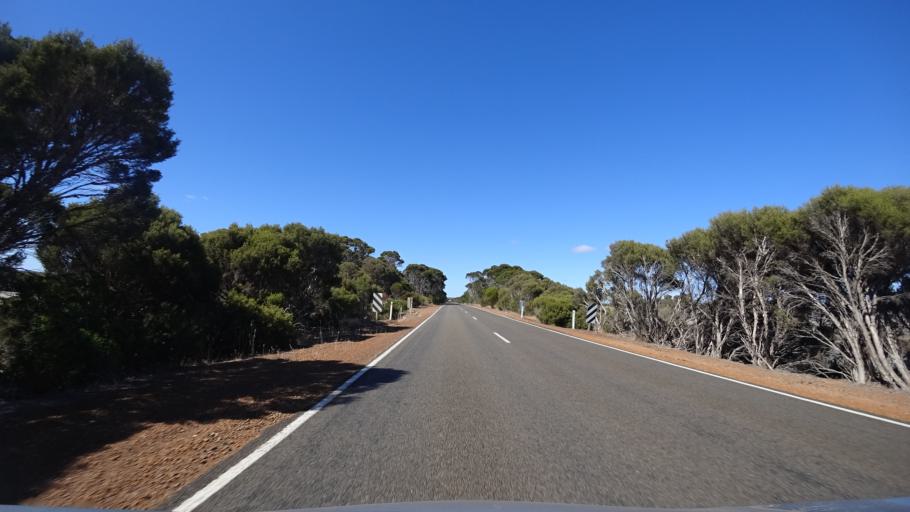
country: AU
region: South Australia
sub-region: Kangaroo Island
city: Kingscote
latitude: -35.7084
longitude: 137.5653
